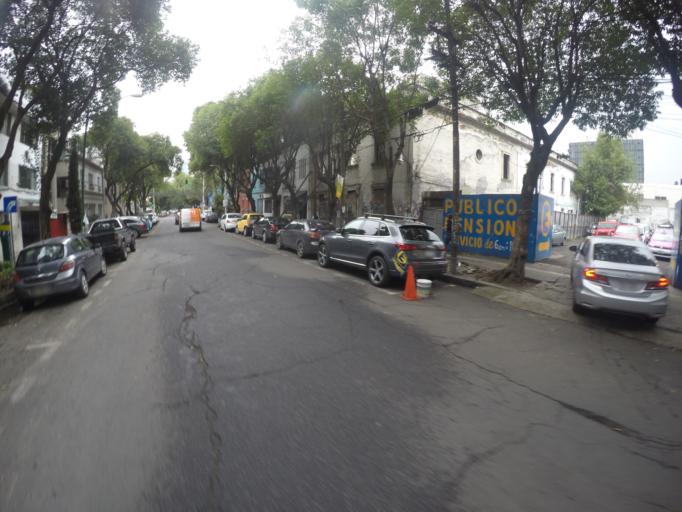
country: MX
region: Mexico City
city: Benito Juarez
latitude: 19.4169
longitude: -99.1704
